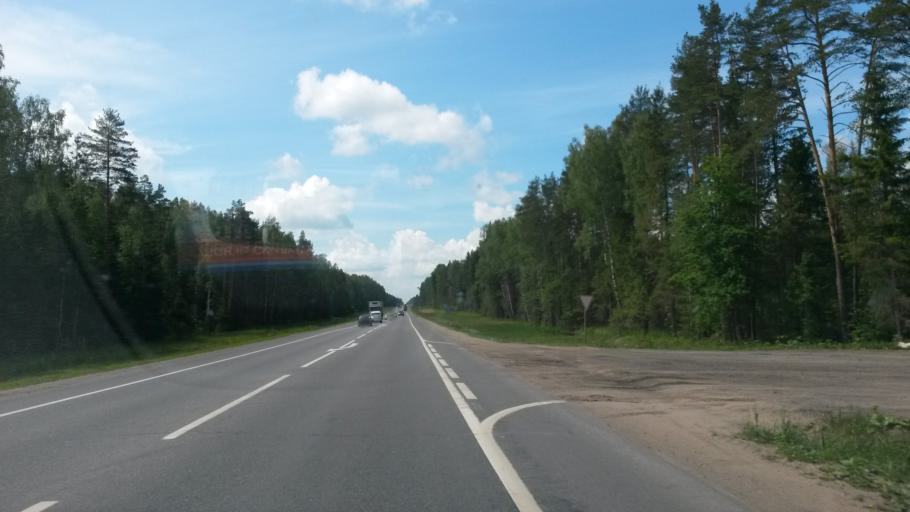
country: RU
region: Jaroslavl
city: Petrovsk
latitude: 56.9258
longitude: 39.1447
